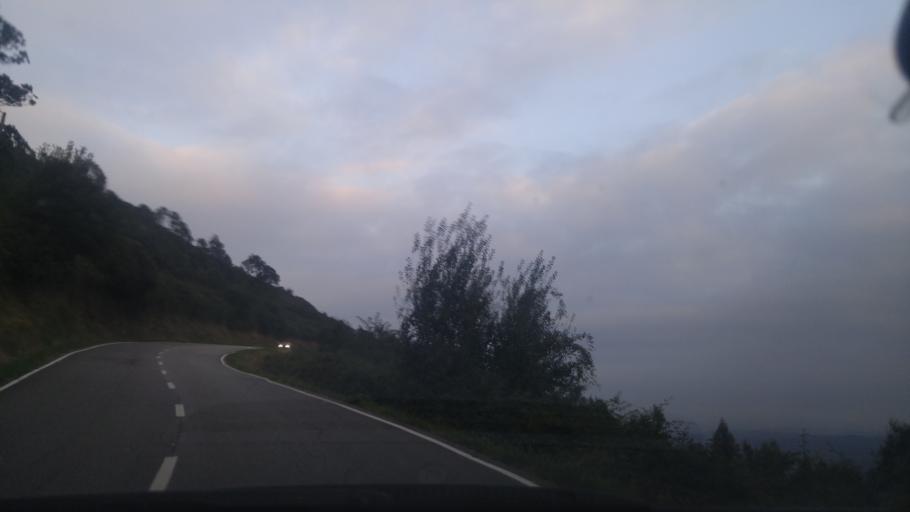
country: ES
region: Asturias
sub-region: Province of Asturias
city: Oviedo
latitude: 43.3808
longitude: -5.8614
